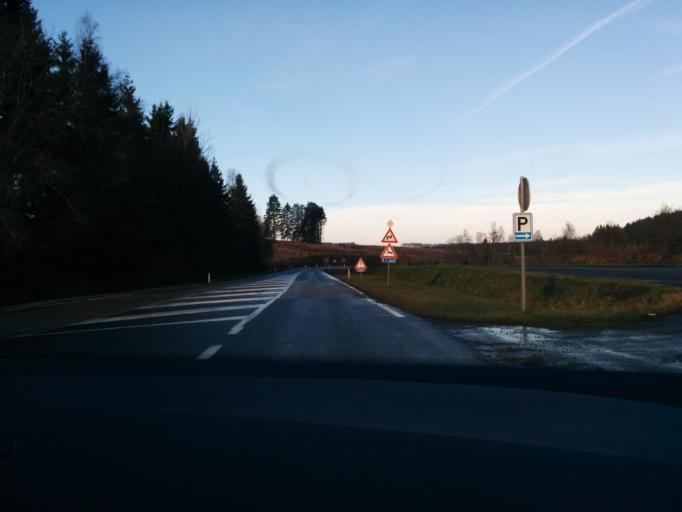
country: BE
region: Wallonia
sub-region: Province du Luxembourg
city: Gouvy
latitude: 50.2228
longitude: 5.9380
